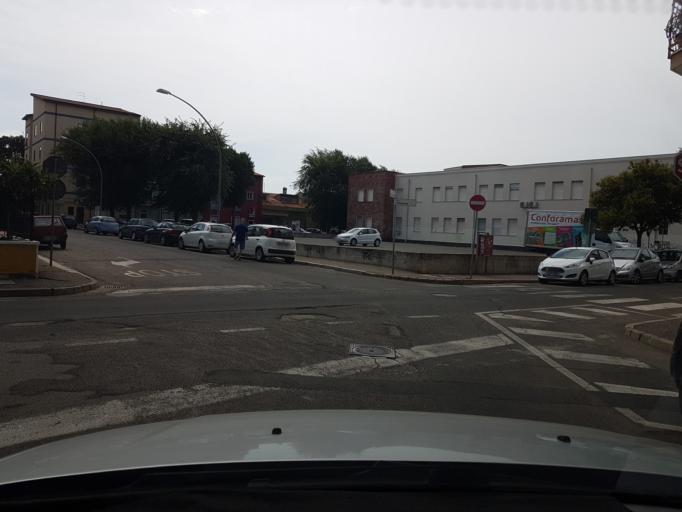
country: IT
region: Sardinia
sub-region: Provincia di Oristano
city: Oristano
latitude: 39.9086
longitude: 8.5952
